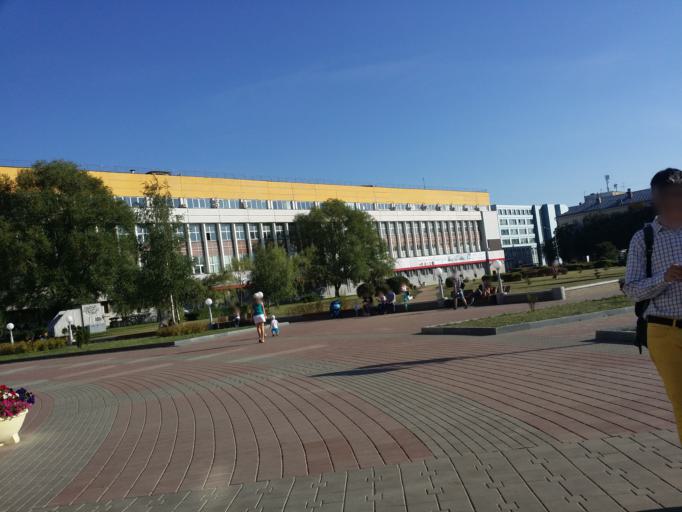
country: BY
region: Minsk
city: Minsk
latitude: 53.9188
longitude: 27.5808
